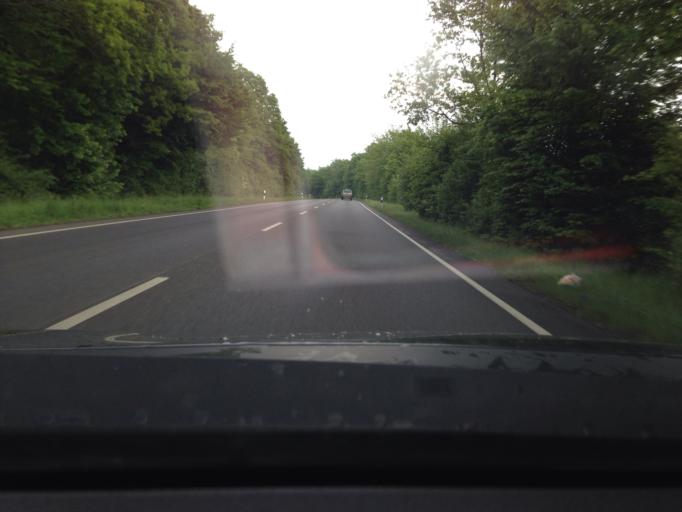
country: DE
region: Hesse
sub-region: Regierungsbezirk Giessen
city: Grossen Buseck
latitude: 50.5910
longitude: 8.7904
